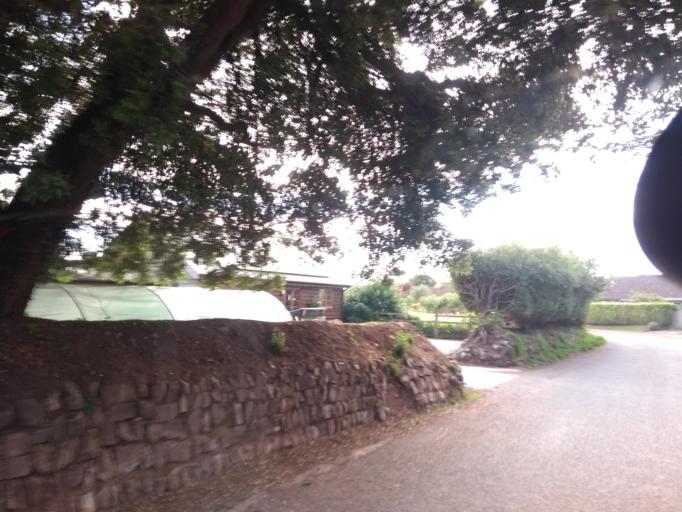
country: GB
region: England
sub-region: Somerset
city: Minehead
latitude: 51.1911
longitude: -3.4401
